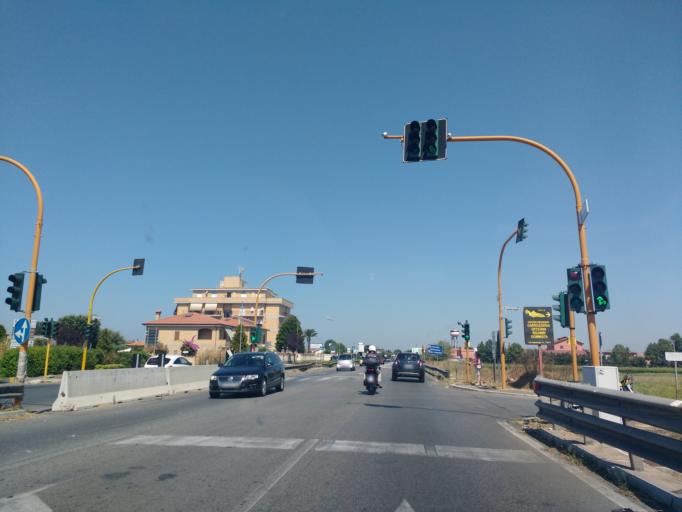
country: IT
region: Latium
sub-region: Citta metropolitana di Roma Capitale
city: Lido di Ostia
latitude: 41.7622
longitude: 12.2674
